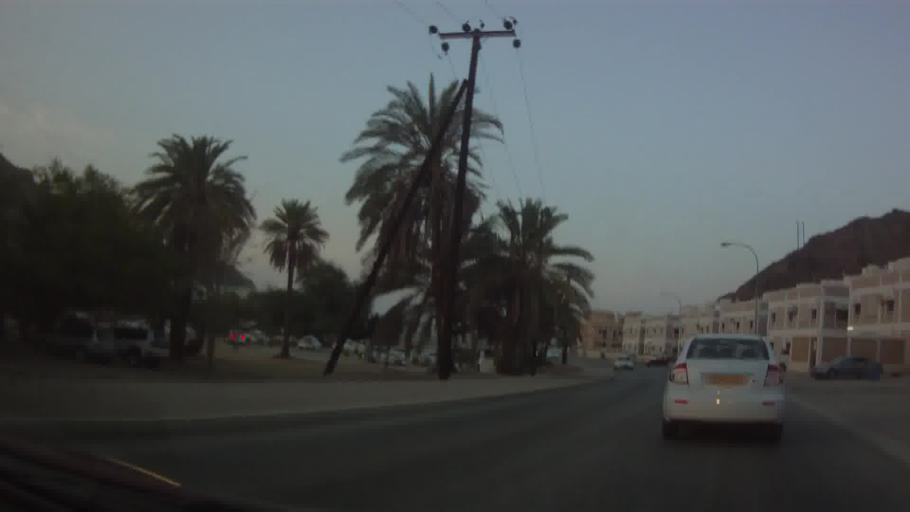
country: OM
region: Muhafazat Masqat
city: Muscat
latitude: 23.6233
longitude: 58.5409
